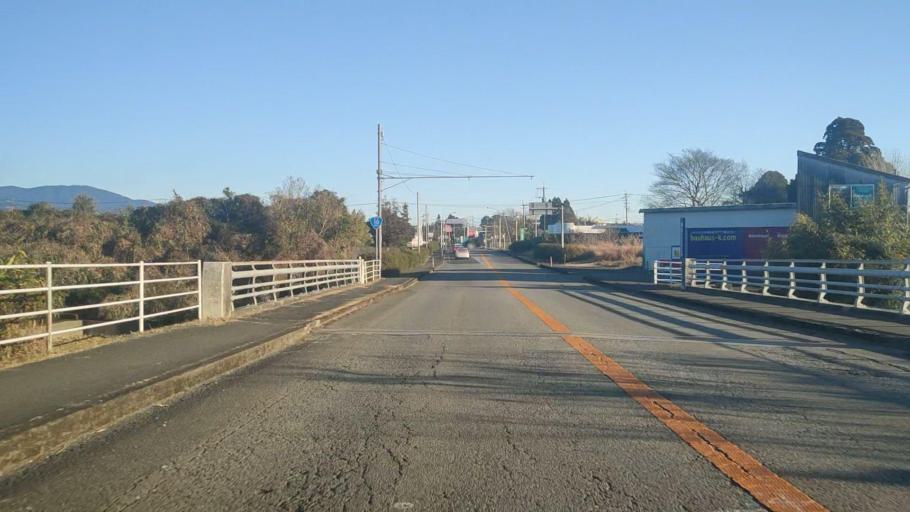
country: JP
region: Miyazaki
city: Takanabe
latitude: 32.1854
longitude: 131.5230
